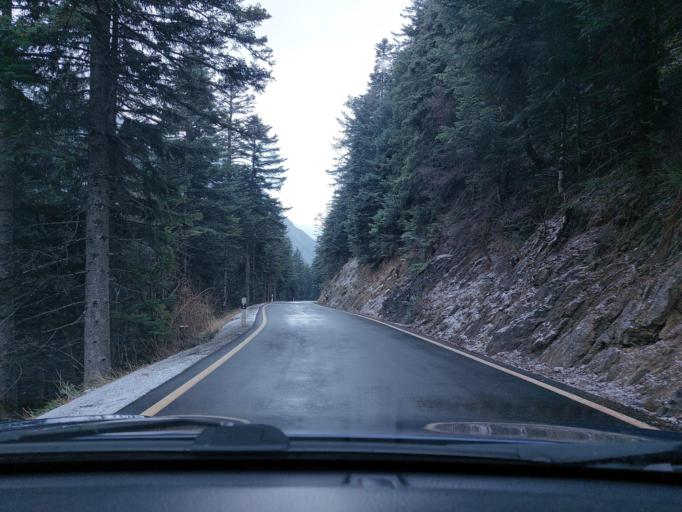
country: CH
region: Valais
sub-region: Sion District
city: Saviese
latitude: 46.2838
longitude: 7.3261
